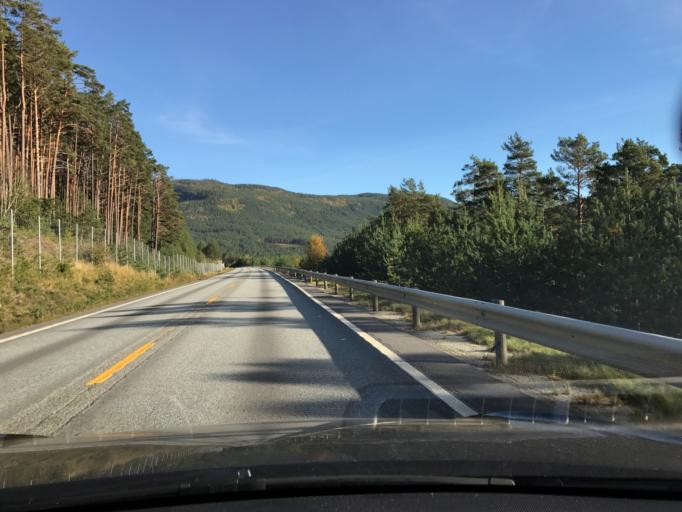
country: NO
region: Sogn og Fjordane
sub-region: Sogndal
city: Sogndalsfjora
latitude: 61.1827
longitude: 7.2694
